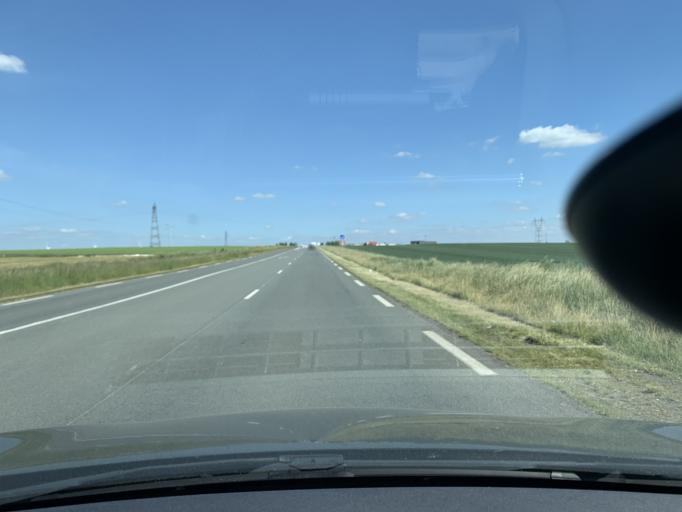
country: FR
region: Nord-Pas-de-Calais
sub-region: Departement du Nord
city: Beauvois-en-Cambresis
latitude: 50.1469
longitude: 3.3558
